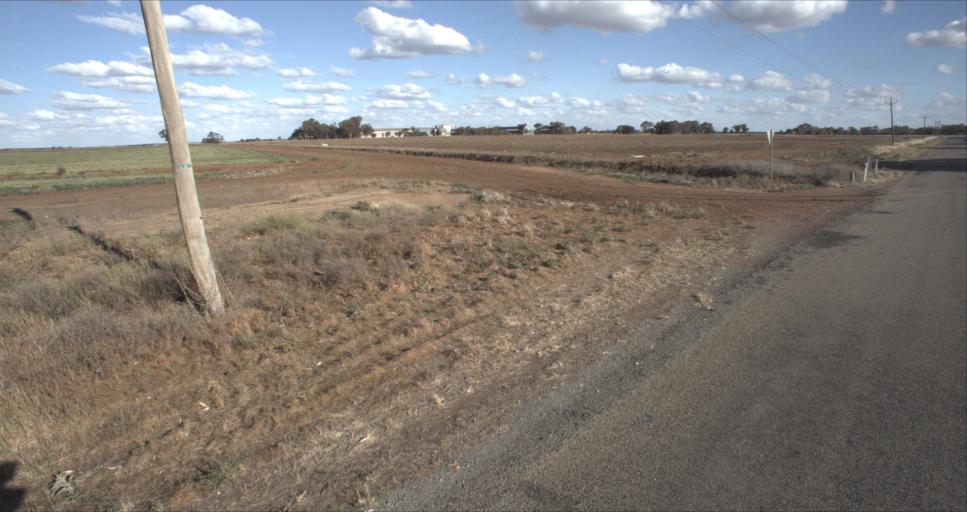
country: AU
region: New South Wales
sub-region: Leeton
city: Leeton
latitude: -34.5490
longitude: 146.2793
